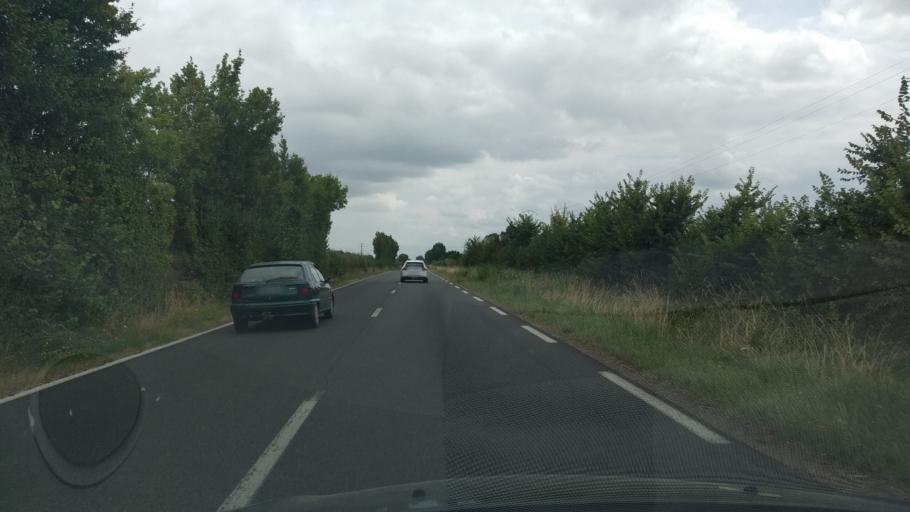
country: FR
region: Poitou-Charentes
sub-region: Departement de la Vienne
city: La Villedieu-du-Clain
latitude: 46.4197
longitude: 0.3828
